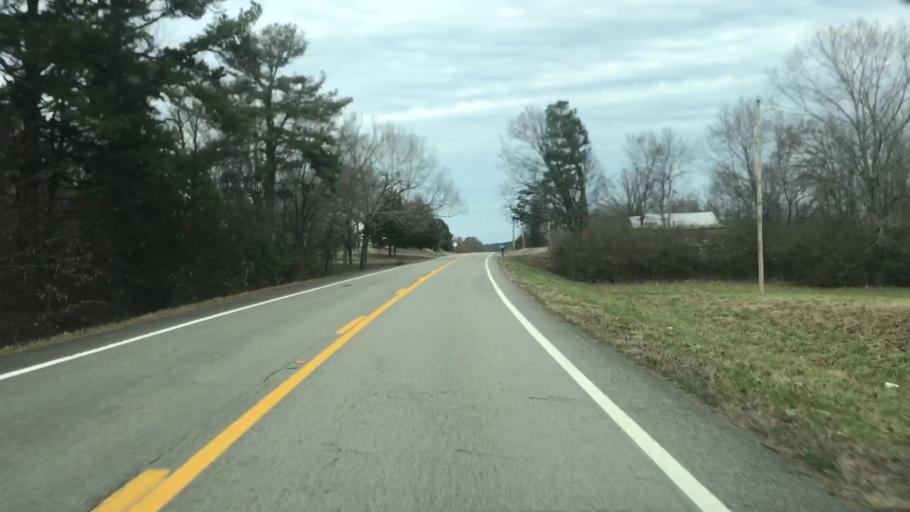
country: US
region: Arkansas
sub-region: Montgomery County
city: Mount Ida
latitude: 34.6518
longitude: -93.7549
